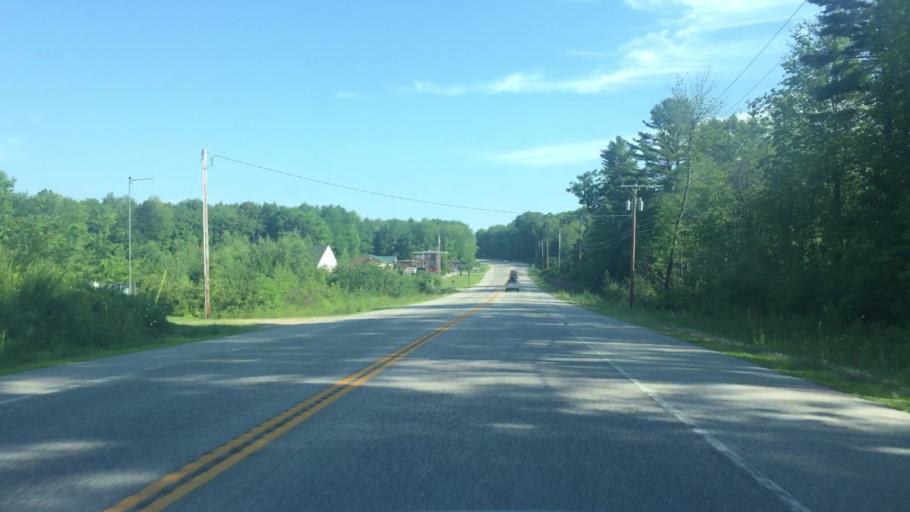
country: US
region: Maine
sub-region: Androscoggin County
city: Poland
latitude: 44.0180
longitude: -70.3634
